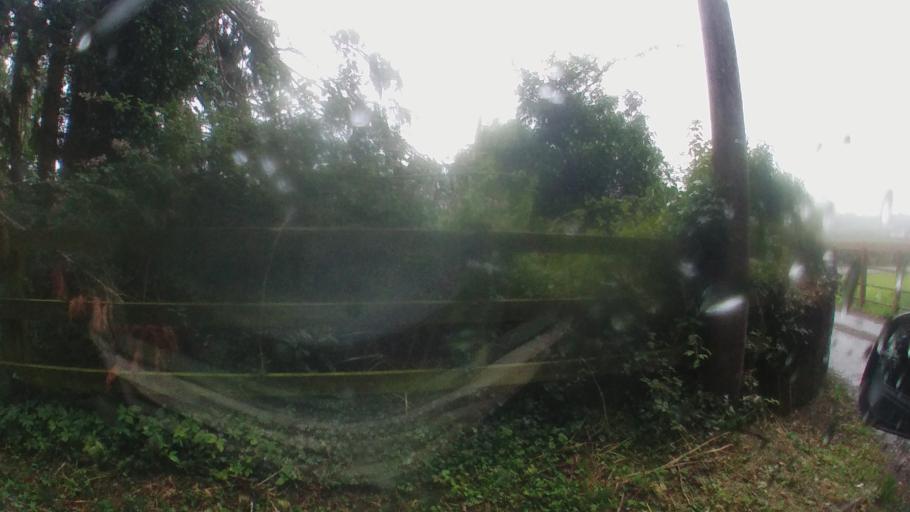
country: IE
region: Leinster
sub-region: Kilkenny
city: Callan
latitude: 52.6624
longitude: -7.4385
